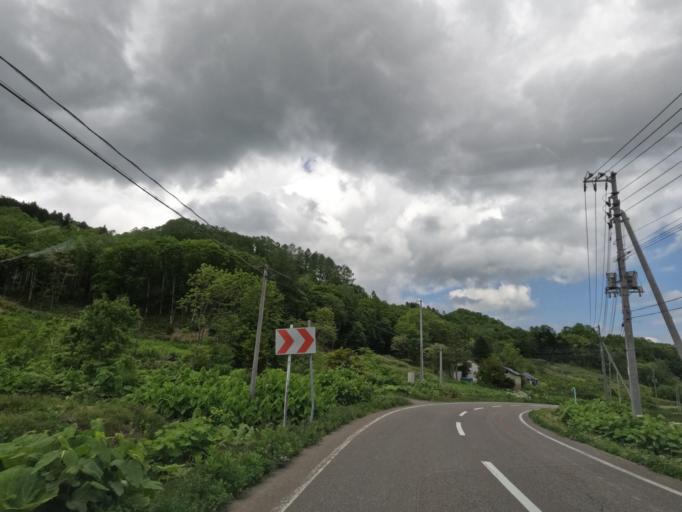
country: JP
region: Hokkaido
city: Takikawa
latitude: 43.5794
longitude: 141.7194
